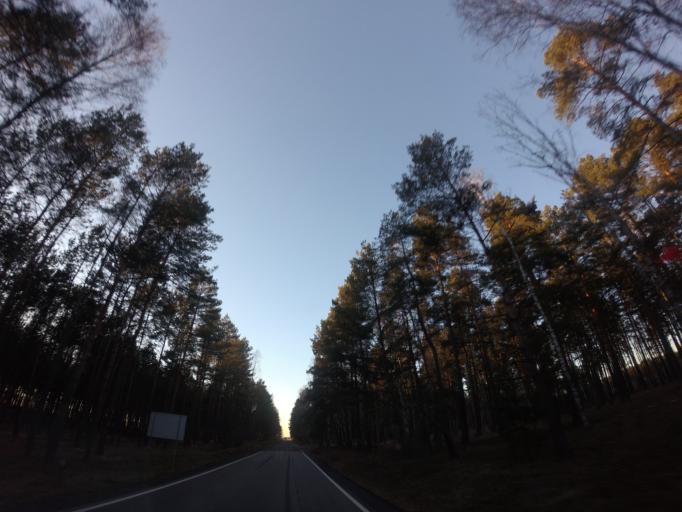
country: PL
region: West Pomeranian Voivodeship
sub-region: Powiat choszczenski
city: Drawno
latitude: 53.1403
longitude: 15.7085
